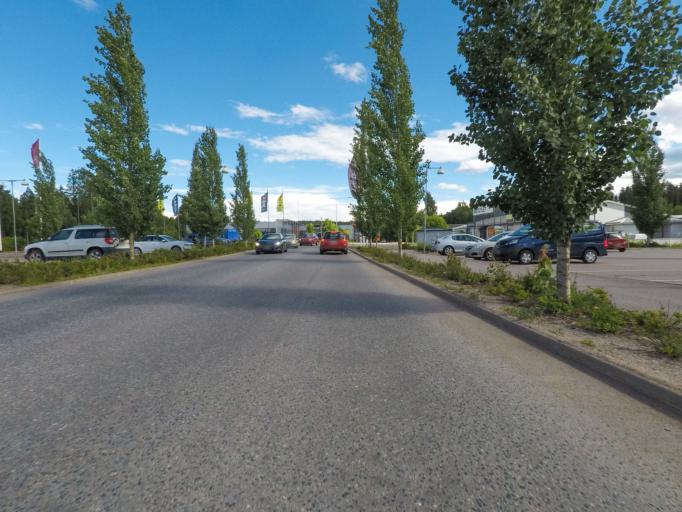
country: FI
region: Paijanne Tavastia
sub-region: Lahti
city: Heinola
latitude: 61.2322
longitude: 26.0451
